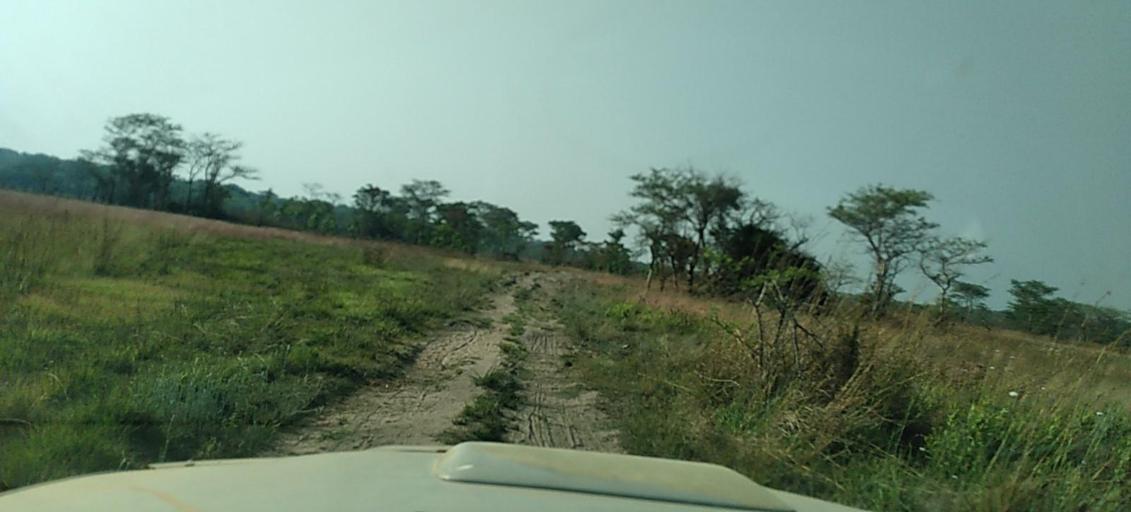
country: ZM
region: North-Western
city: Kasempa
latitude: -13.1878
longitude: 25.9682
